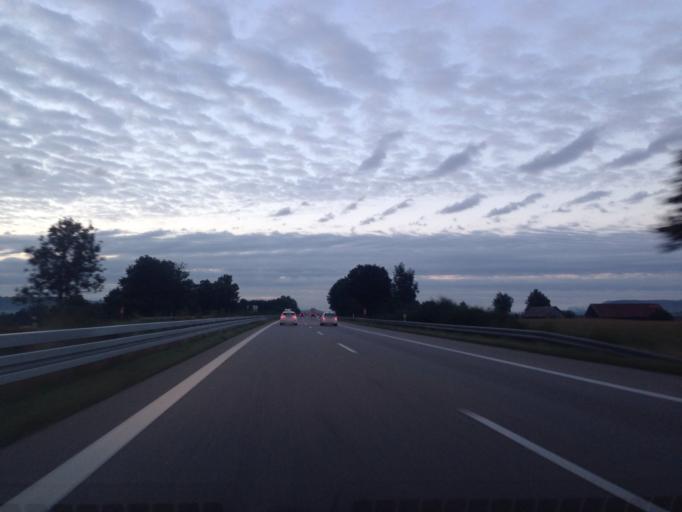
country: DE
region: Bavaria
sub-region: Swabia
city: Wolfertschwenden
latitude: 47.9028
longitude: 10.2424
